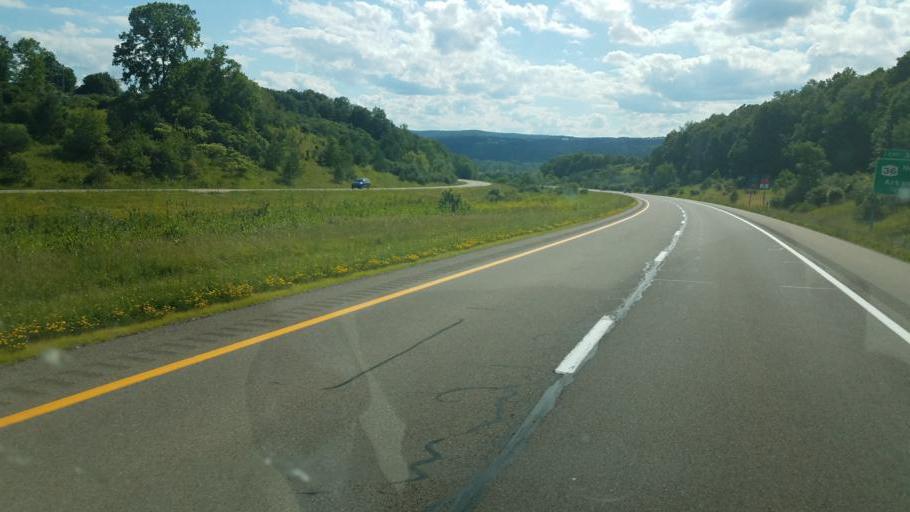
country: US
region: New York
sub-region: Steuben County
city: Hornell
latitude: 42.3803
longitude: -77.6619
